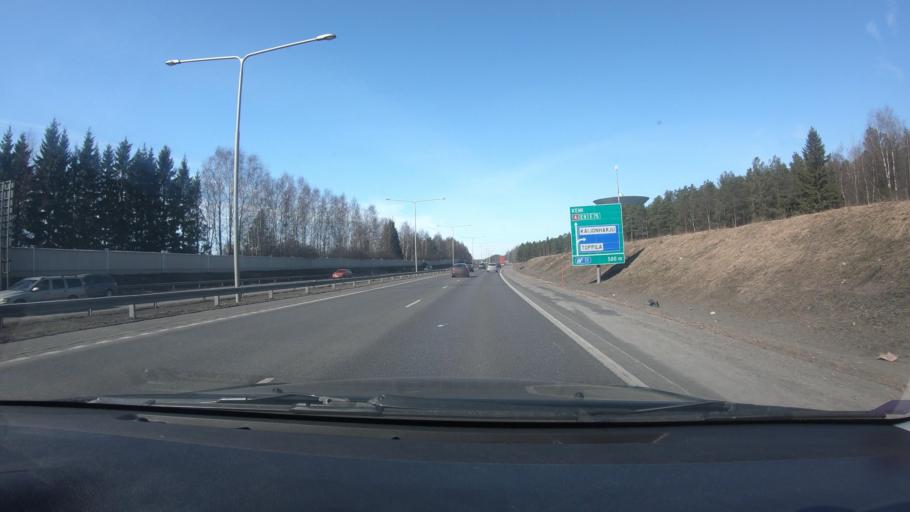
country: FI
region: Northern Ostrobothnia
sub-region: Oulu
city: Oulu
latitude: 65.0340
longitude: 25.4902
